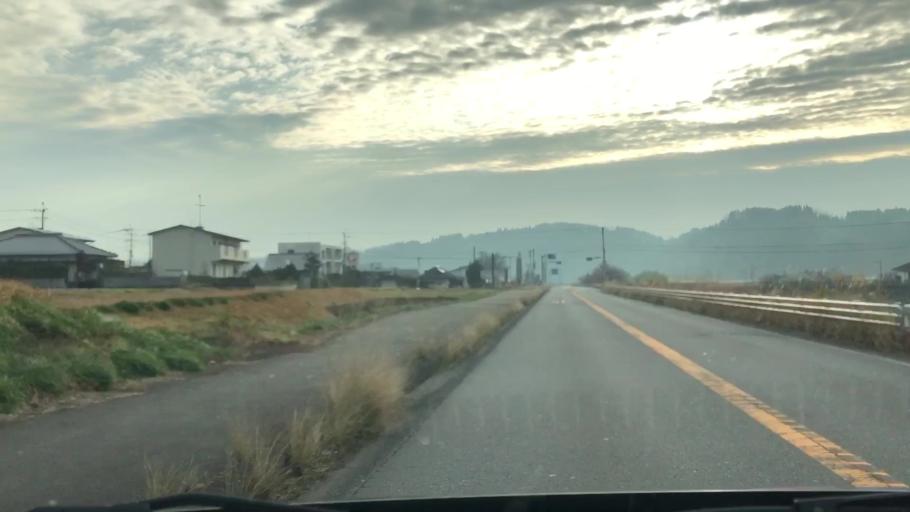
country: JP
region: Oita
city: Takedamachi
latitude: 32.9670
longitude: 131.4796
